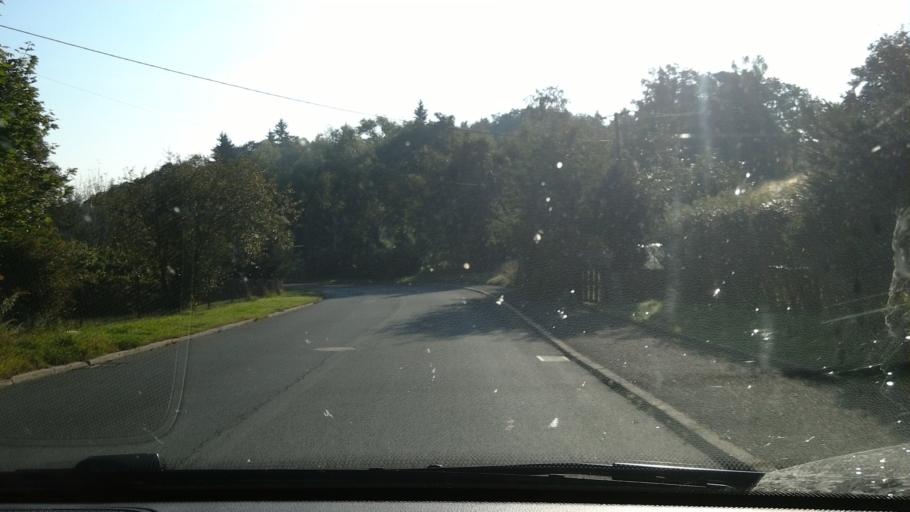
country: PL
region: Lower Silesian Voivodeship
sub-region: Powiat jeleniogorski
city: Szklarska Poreba
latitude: 50.8413
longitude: 15.5564
